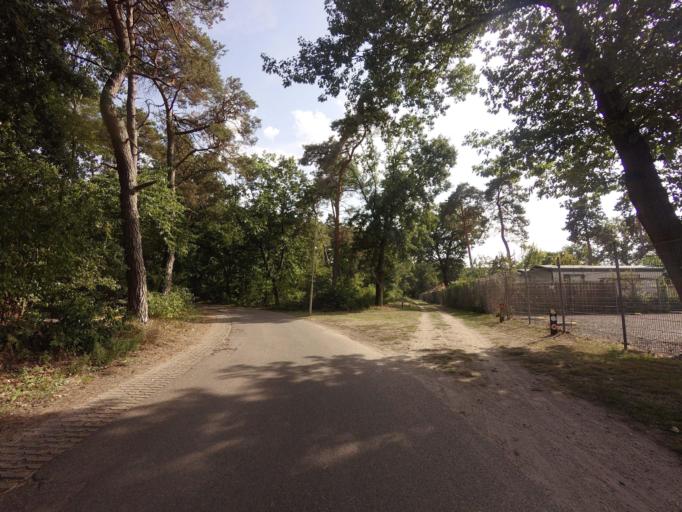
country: NL
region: North Brabant
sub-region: Gemeente Someren
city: Someren
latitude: 51.3997
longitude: 5.6764
